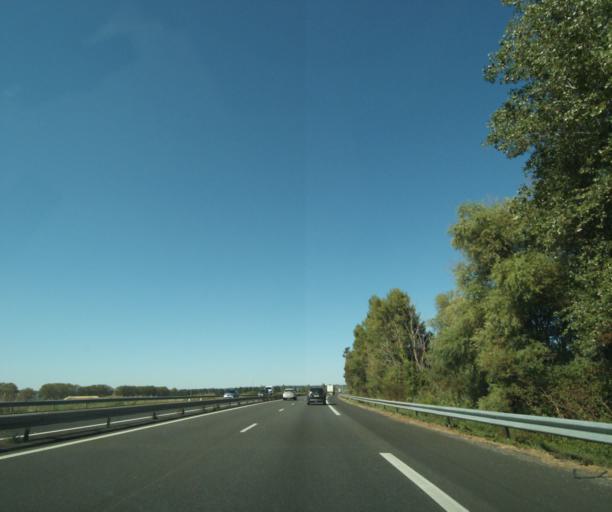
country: FR
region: Languedoc-Roussillon
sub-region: Departement du Gard
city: Bellegarde
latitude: 43.7147
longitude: 4.5127
